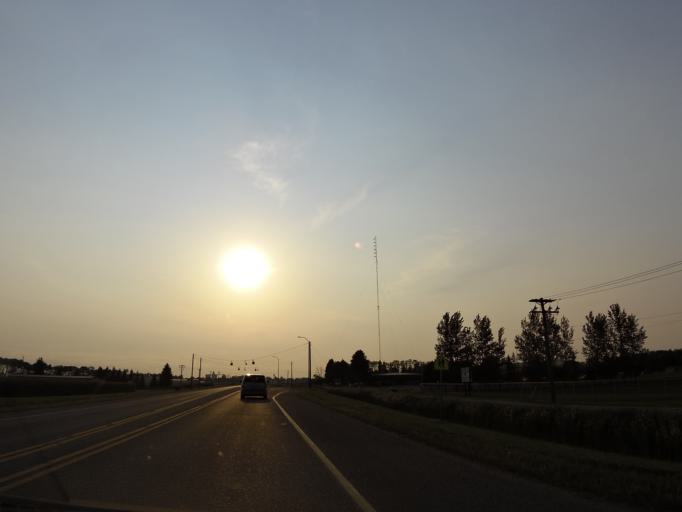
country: US
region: North Dakota
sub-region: Traill County
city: Mayville
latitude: 47.4985
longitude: -97.3465
